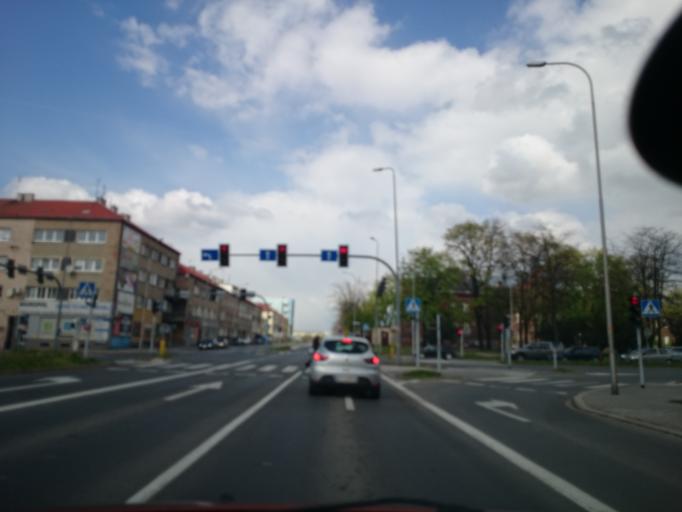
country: PL
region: Opole Voivodeship
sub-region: Powiat opolski
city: Opole
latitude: 50.6678
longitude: 17.9422
